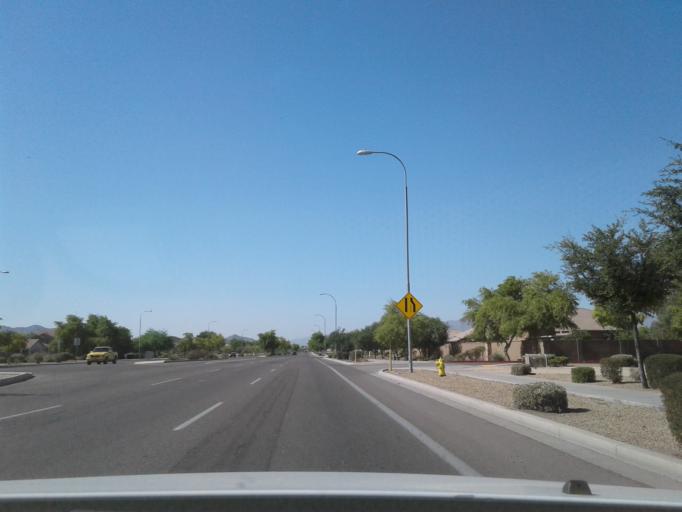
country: US
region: Arizona
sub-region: Maricopa County
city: Laveen
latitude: 33.3905
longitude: -112.1684
